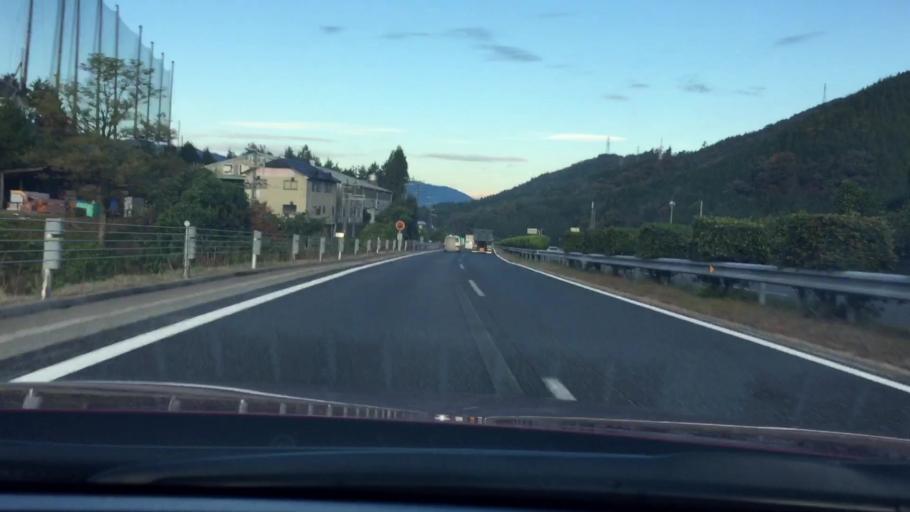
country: JP
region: Hyogo
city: Yamazakicho-nakabirose
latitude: 34.9923
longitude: 134.5750
